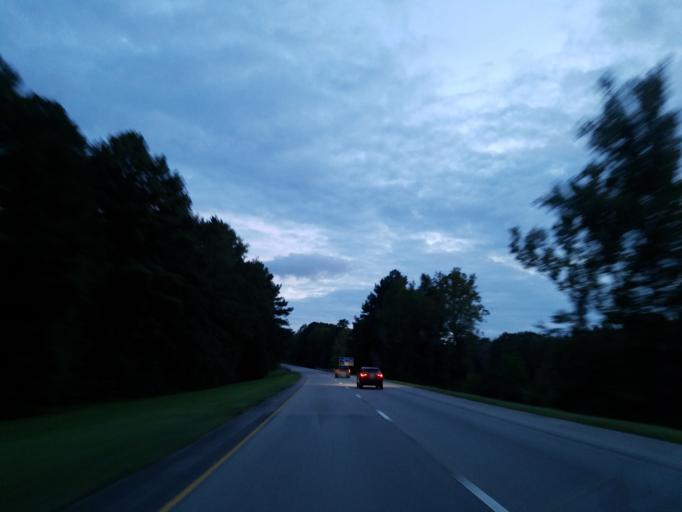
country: US
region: Mississippi
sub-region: Clarke County
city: Stonewall
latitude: 32.1762
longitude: -88.8660
